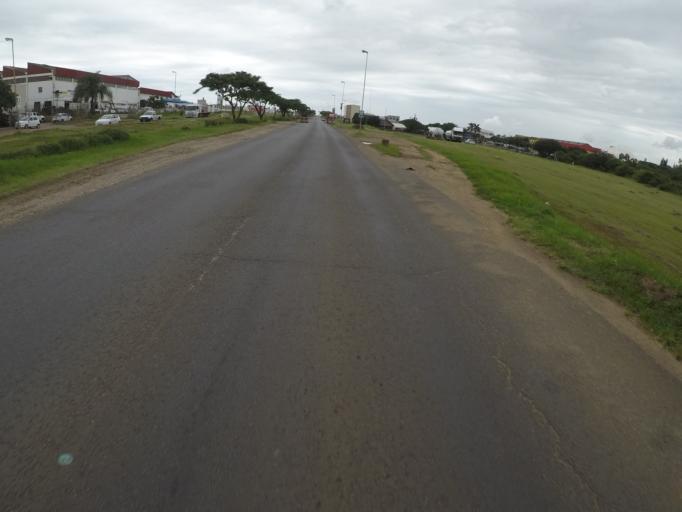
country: ZA
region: KwaZulu-Natal
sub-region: uThungulu District Municipality
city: Empangeni
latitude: -28.7720
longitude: 31.9020
